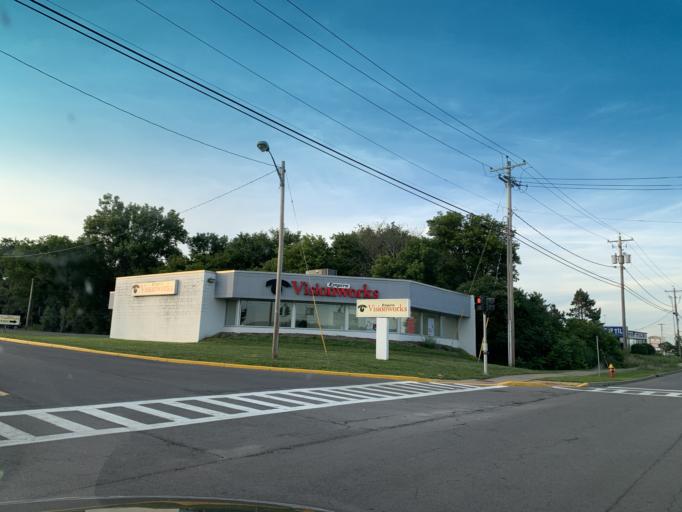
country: US
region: New York
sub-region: Oneida County
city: New Hartford
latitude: 43.0851
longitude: -75.3180
